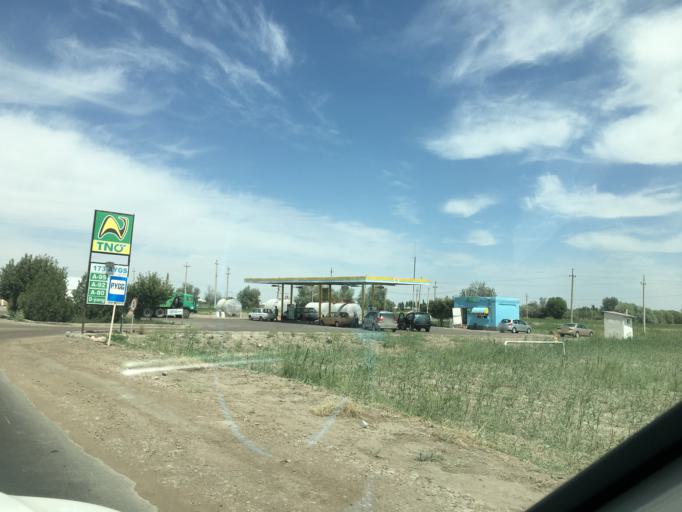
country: TM
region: Dasoguz
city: Tagta
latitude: 41.6923
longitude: 59.9297
